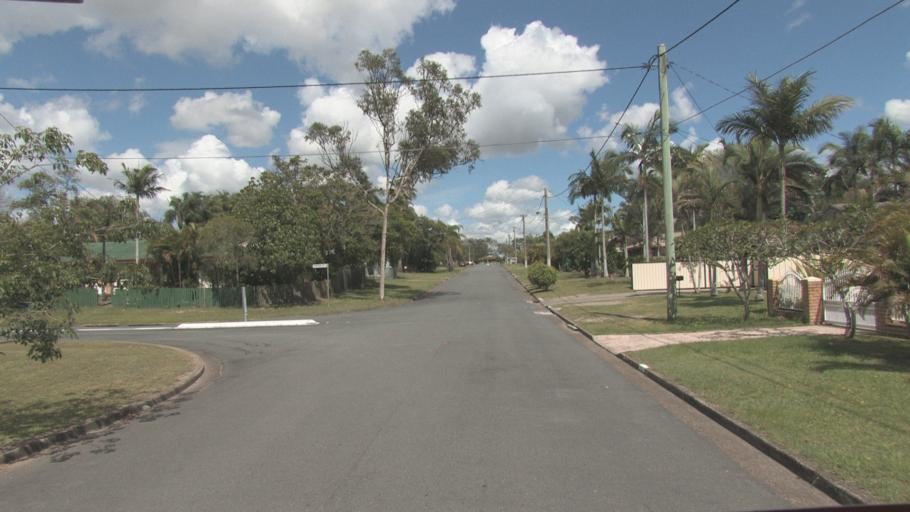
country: AU
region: Queensland
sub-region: Logan
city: Waterford West
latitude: -27.6709
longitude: 153.1270
